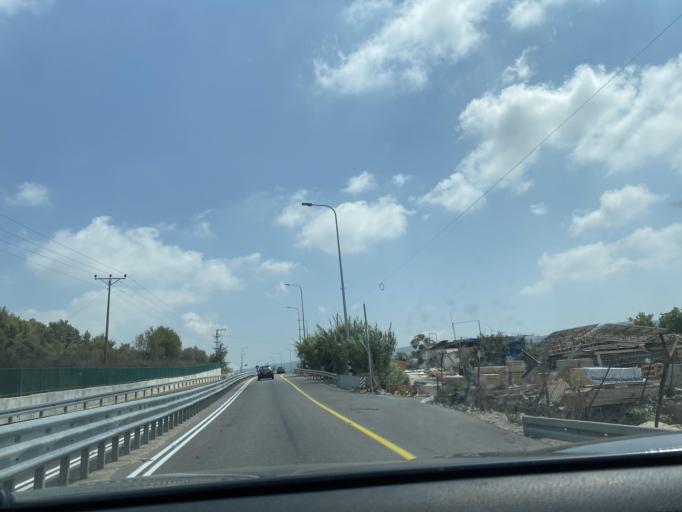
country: IL
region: Northern District
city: Kefar Weradim
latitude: 33.0014
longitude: 35.2983
